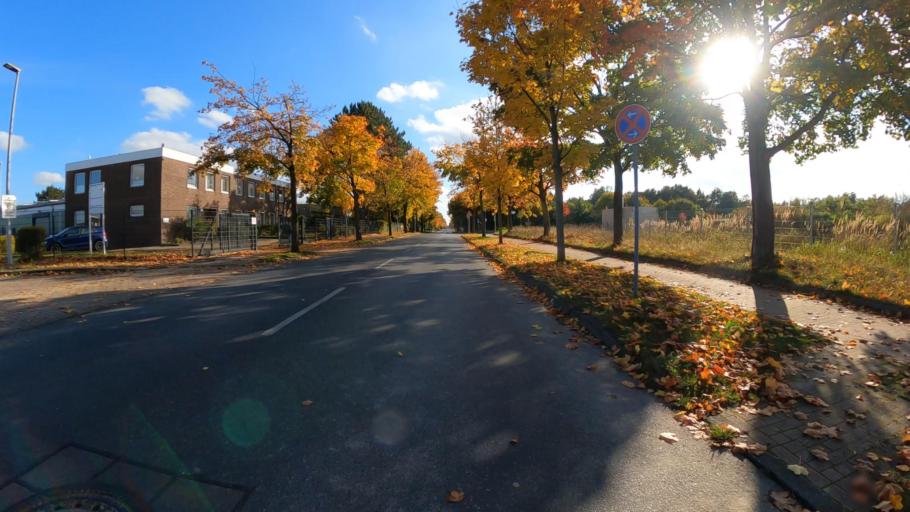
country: DE
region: Schleswig-Holstein
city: Delingsdorf
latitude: 53.6903
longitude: 10.2555
